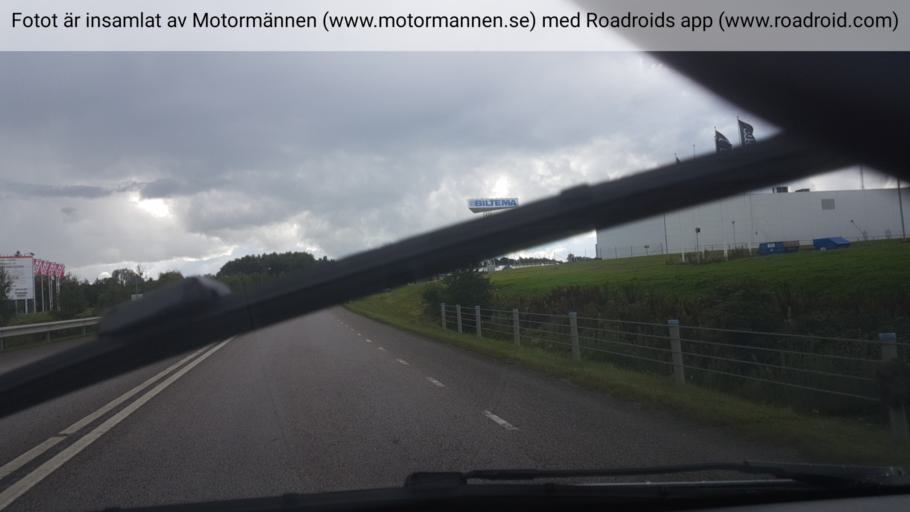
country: SE
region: Vaestra Goetaland
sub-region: Skovde Kommun
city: Skoevde
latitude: 58.4103
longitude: 13.8799
